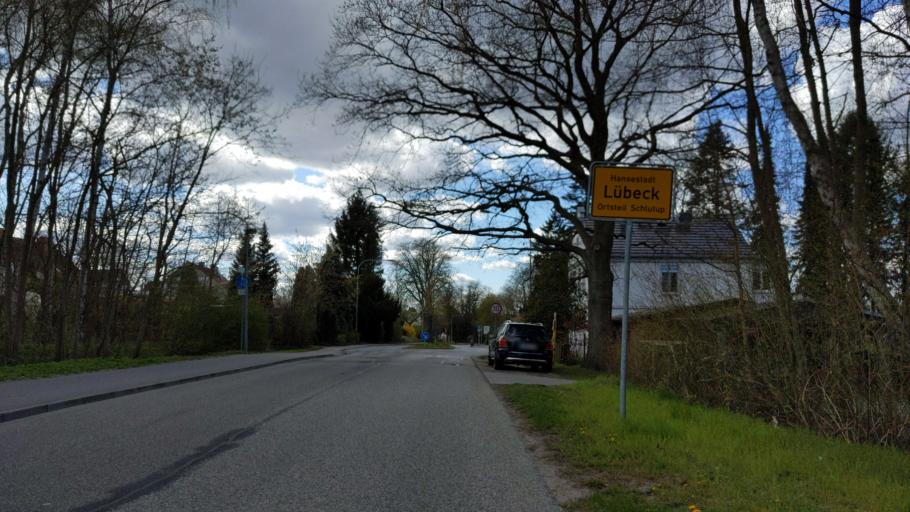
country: DE
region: Mecklenburg-Vorpommern
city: Selmsdorf
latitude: 53.8840
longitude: 10.8086
